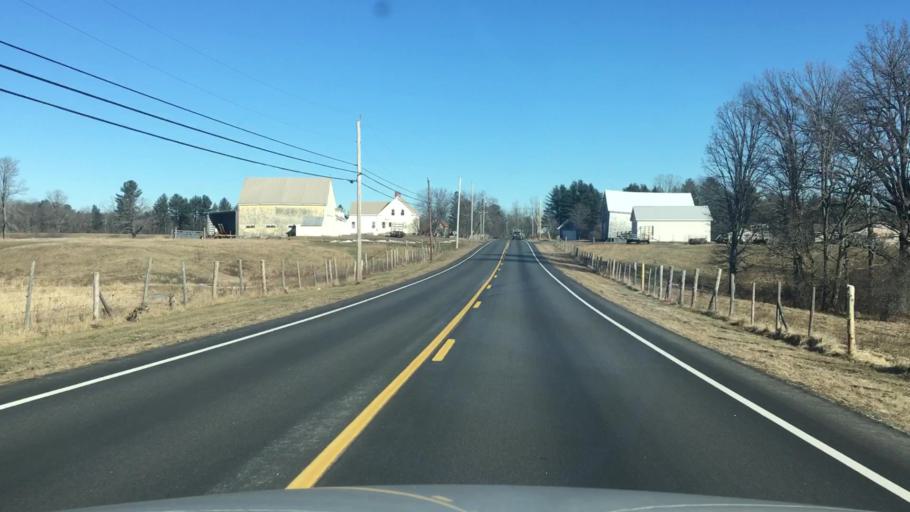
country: US
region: Maine
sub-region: Kennebec County
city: Benton
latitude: 44.6000
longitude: -69.5420
